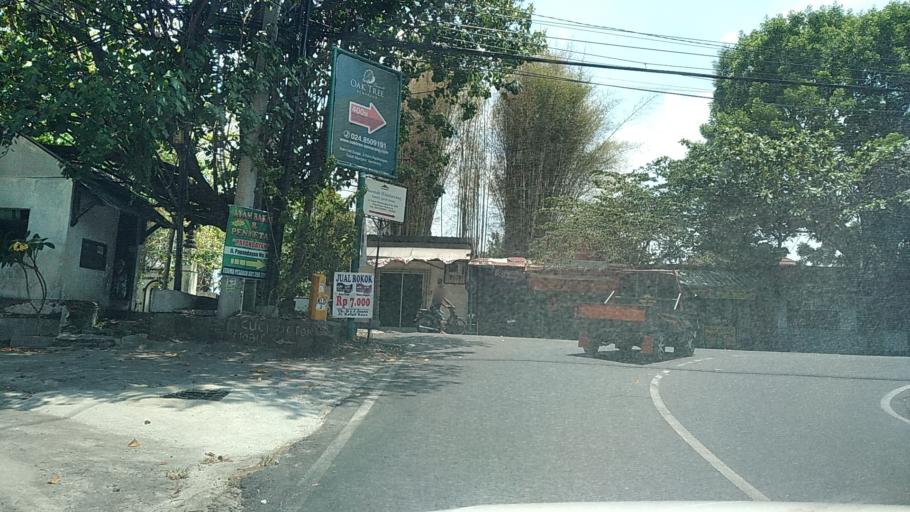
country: ID
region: Central Java
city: Semarang
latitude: -7.0139
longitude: 110.4128
